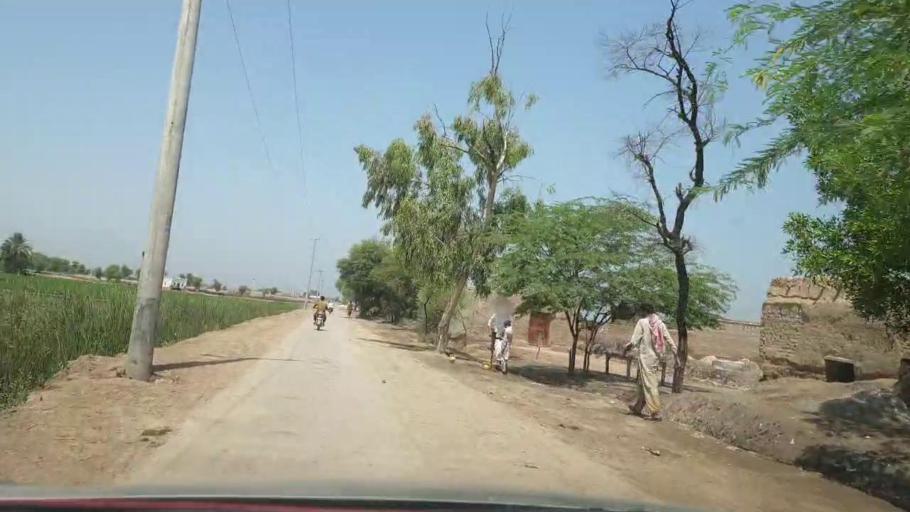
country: PK
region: Sindh
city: Warah
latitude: 27.4797
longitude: 67.7560
